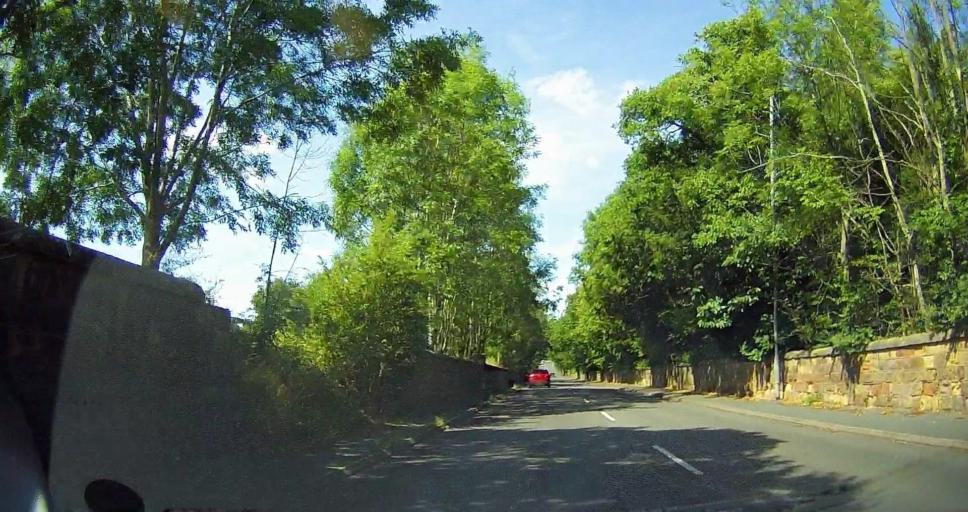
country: GB
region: England
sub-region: Staffordshire
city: Codsall
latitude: 52.6074
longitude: -2.1959
